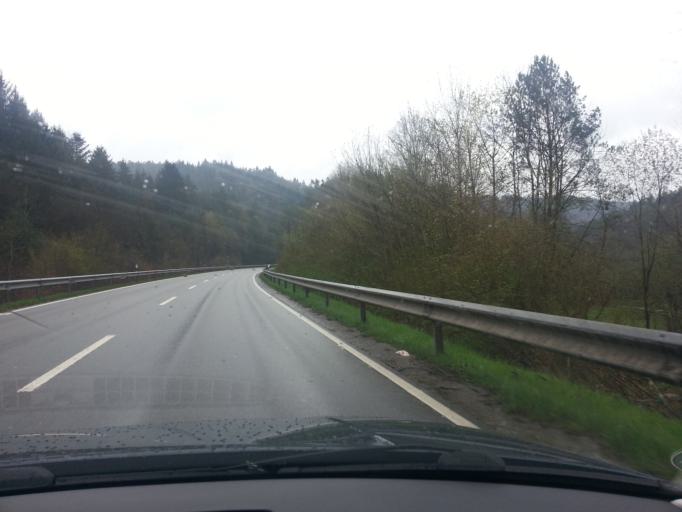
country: DE
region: Rheinland-Pfalz
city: Munchweiler an der Rodalbe
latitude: 49.2214
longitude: 7.6945
